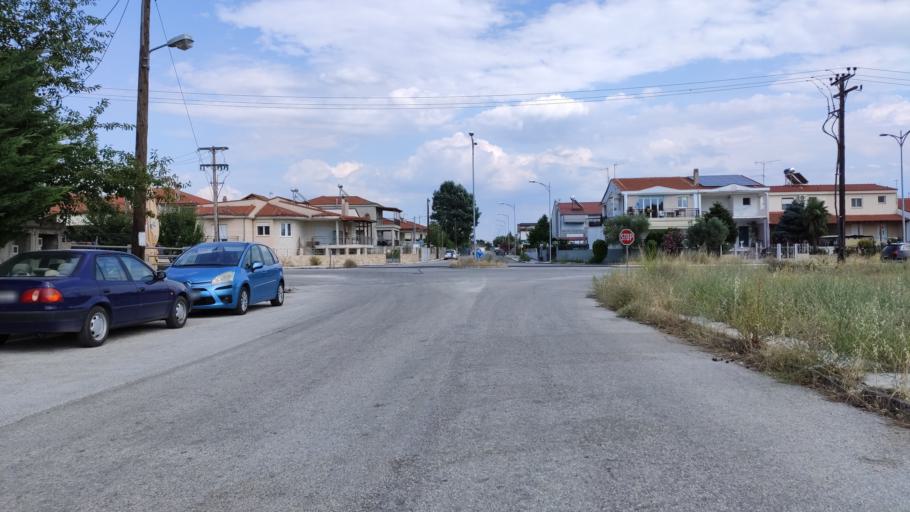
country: GR
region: East Macedonia and Thrace
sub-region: Nomos Rodopis
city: Komotini
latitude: 41.1291
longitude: 25.3951
